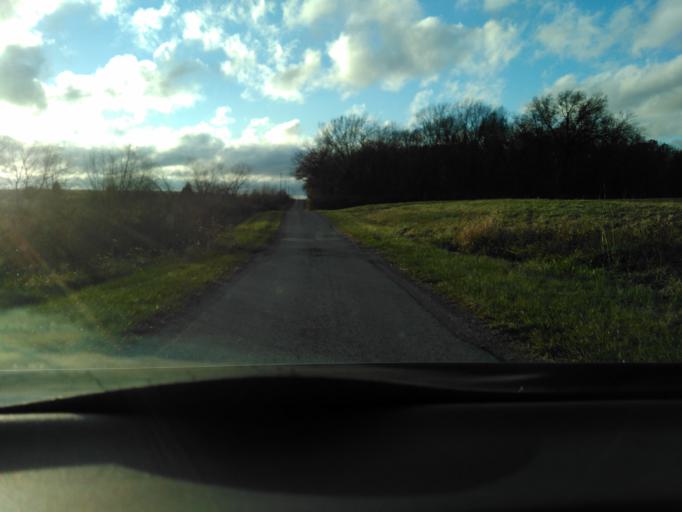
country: US
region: Illinois
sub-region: Effingham County
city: Altamont
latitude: 38.9511
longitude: -88.6988
